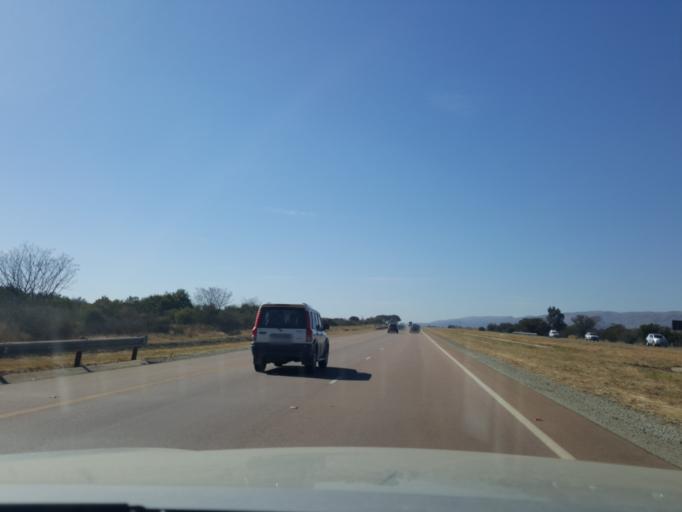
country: ZA
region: North-West
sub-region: Bojanala Platinum District Municipality
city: Brits
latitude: -25.7369
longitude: 27.6098
